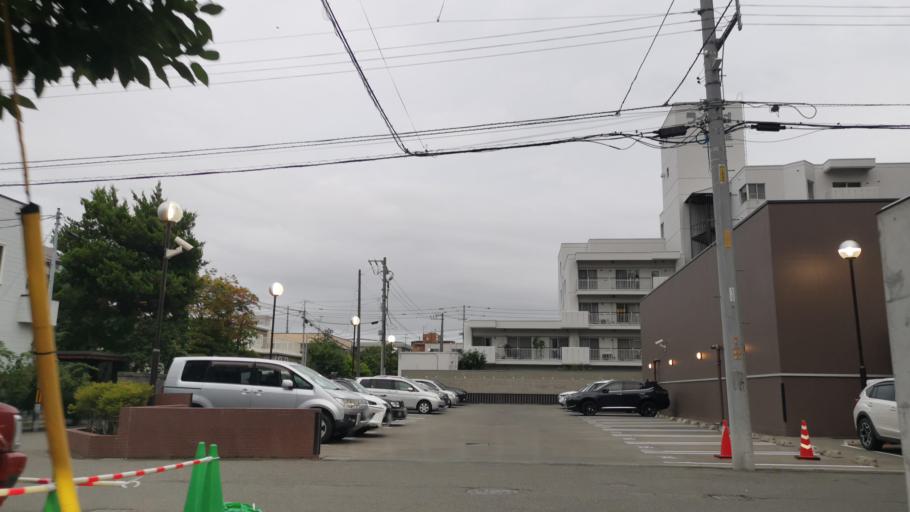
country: JP
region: Hokkaido
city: Sapporo
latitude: 43.0480
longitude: 141.3267
